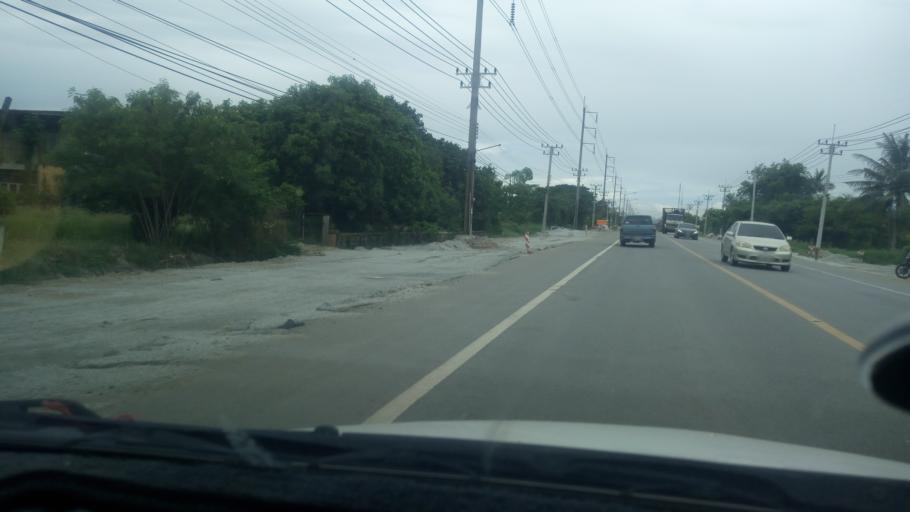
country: TH
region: Chon Buri
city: Phanat Nikhom
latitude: 13.5053
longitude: 101.1589
